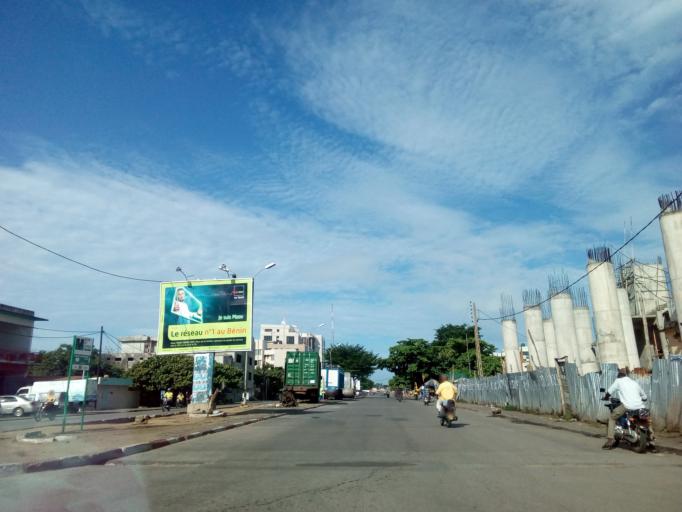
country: BJ
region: Littoral
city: Cotonou
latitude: 6.3609
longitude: 2.4220
